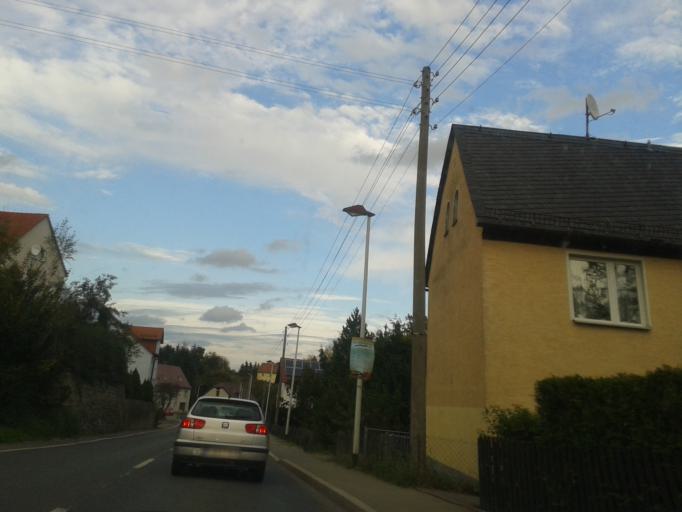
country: DE
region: Saxony
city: Niederschona
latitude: 51.0057
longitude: 13.4660
